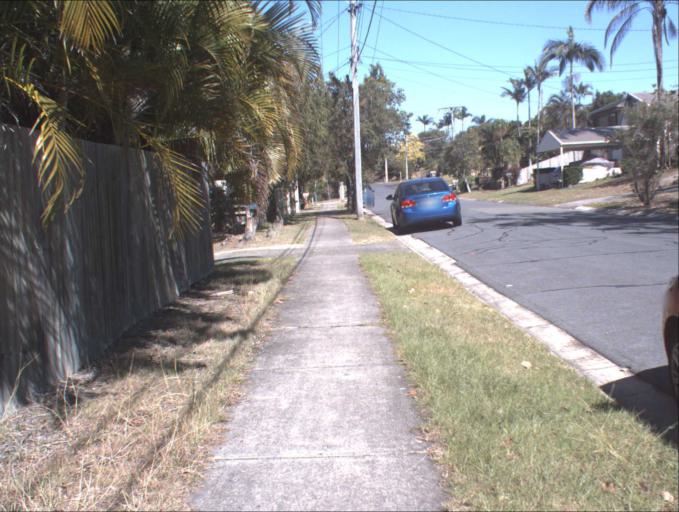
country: AU
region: Queensland
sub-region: Logan
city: Springwood
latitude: -27.6055
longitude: 153.1231
